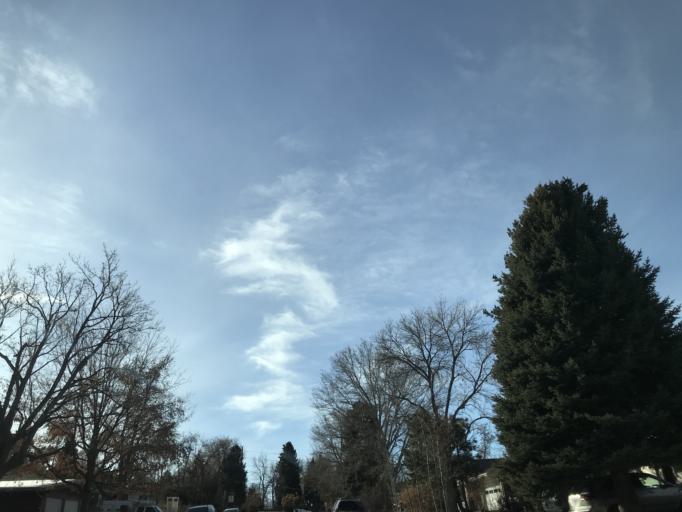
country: US
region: Colorado
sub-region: Arapahoe County
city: Littleton
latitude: 39.6090
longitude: -105.0093
